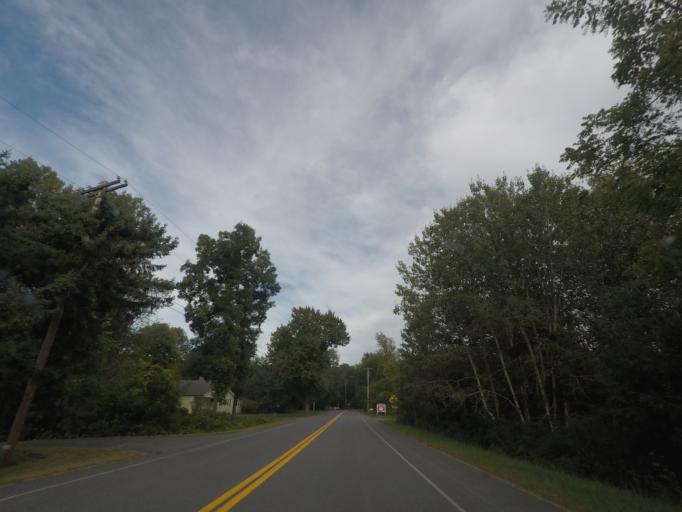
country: US
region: New York
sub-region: Rensselaer County
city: East Greenbush
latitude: 42.6010
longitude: -73.6794
